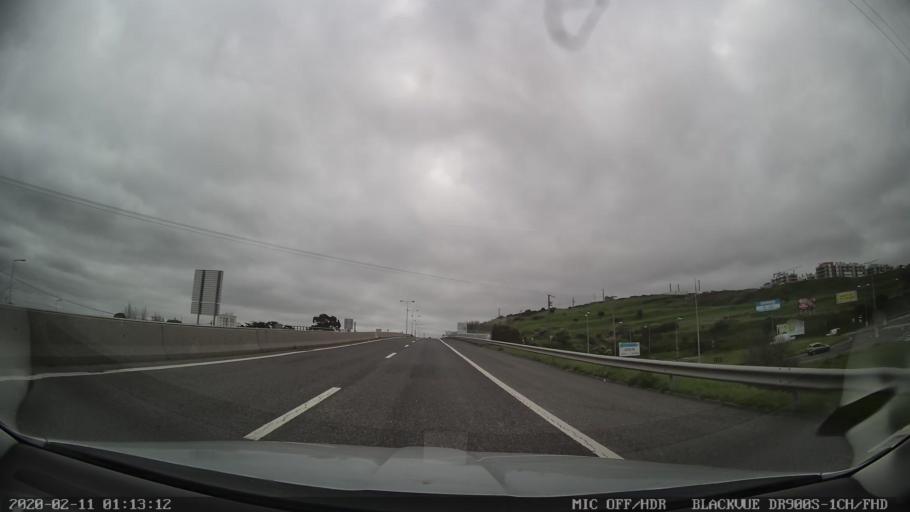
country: PT
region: Lisbon
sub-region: Odivelas
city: Ramada
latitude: 38.8167
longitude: -9.1853
